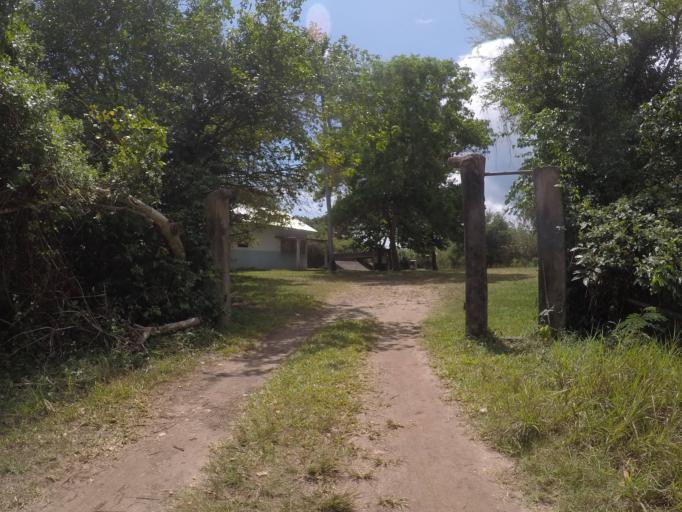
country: TZ
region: Zanzibar North
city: Mkokotoni
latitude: -5.9874
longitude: 39.1858
